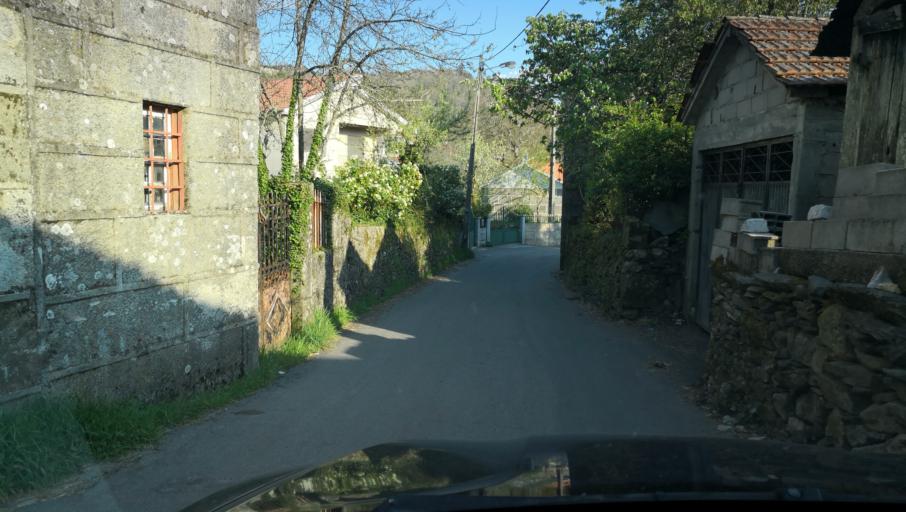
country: PT
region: Vila Real
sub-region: Vila Real
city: Vila Real
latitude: 41.2988
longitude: -7.8365
